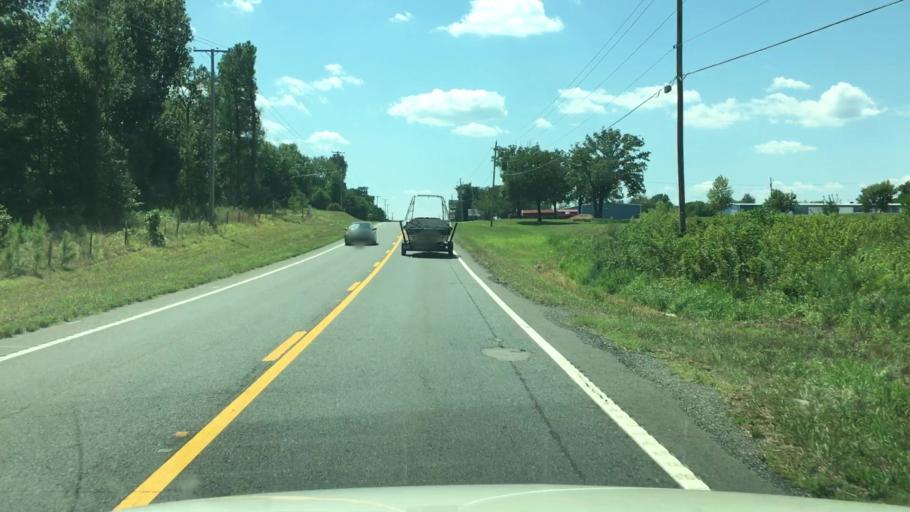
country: US
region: Arkansas
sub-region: Garland County
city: Piney
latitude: 34.5105
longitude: -93.2120
